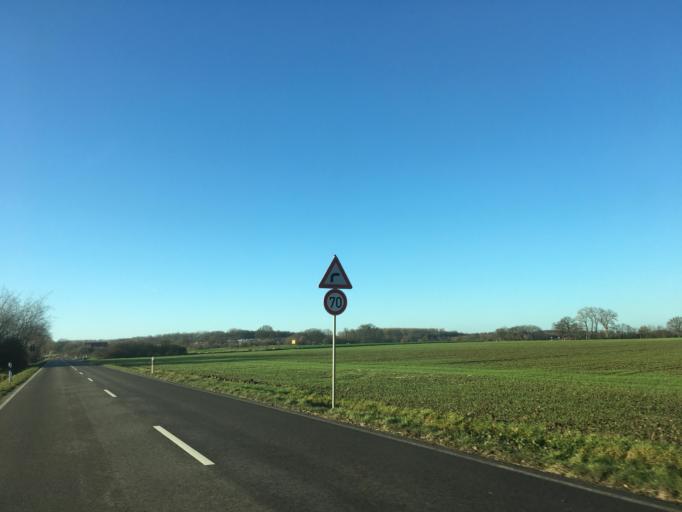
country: DE
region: North Rhine-Westphalia
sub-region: Regierungsbezirk Munster
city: Dulmen
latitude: 51.8251
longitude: 7.3354
